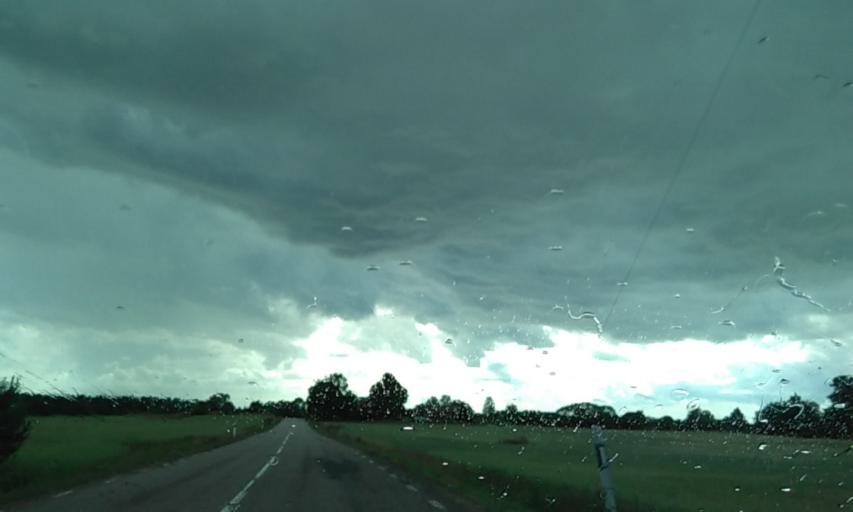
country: SE
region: Vaestra Goetaland
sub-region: Vara Kommun
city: Vara
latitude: 58.4807
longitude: 12.8755
